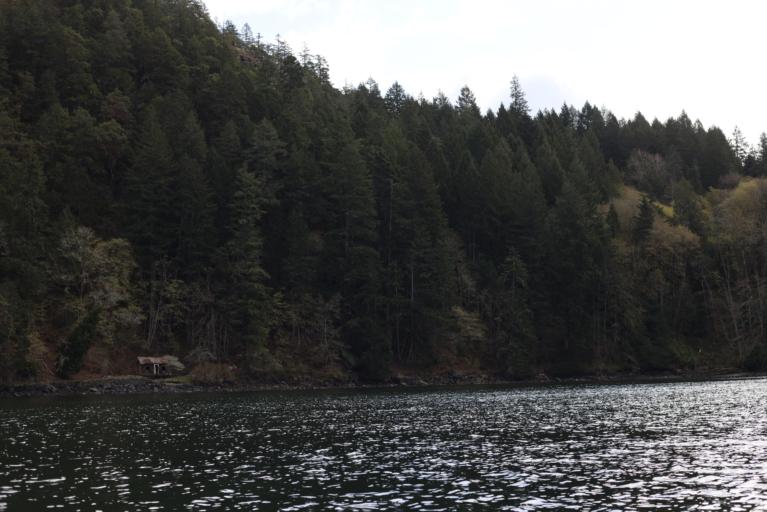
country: CA
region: British Columbia
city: Langford
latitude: 48.4975
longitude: -123.5504
